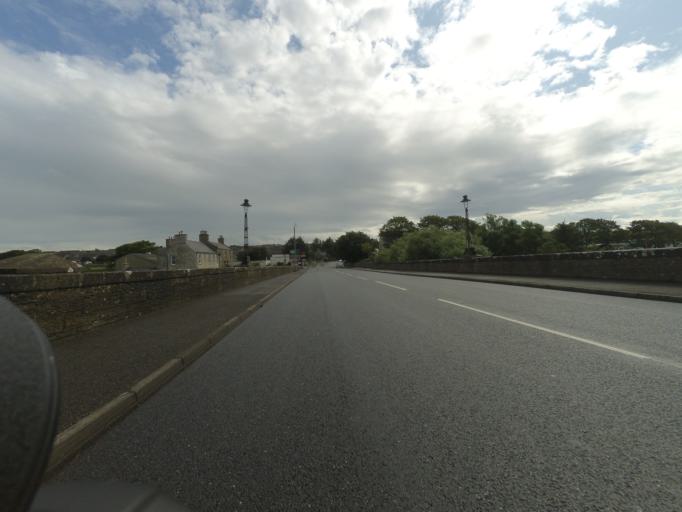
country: GB
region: Scotland
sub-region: Highland
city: Thurso
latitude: 58.5925
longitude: -3.5193
